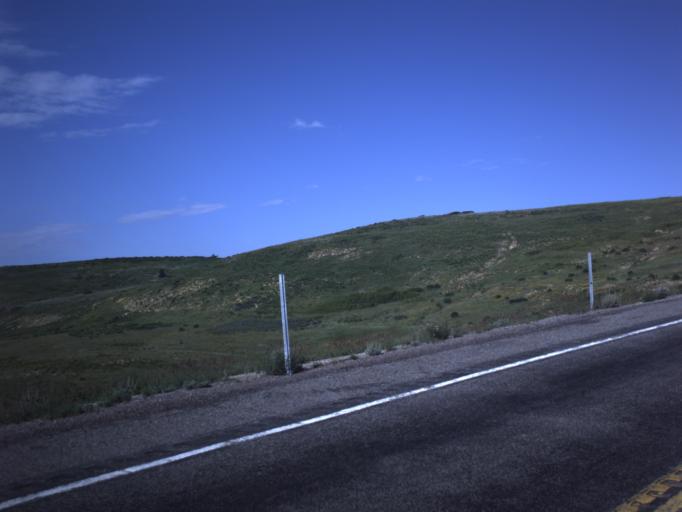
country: US
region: Utah
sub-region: Sanpete County
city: Fairview
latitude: 39.6145
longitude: -111.3060
